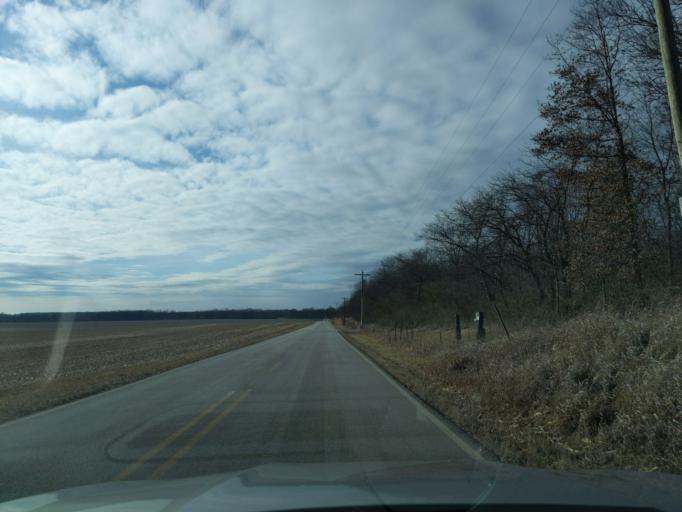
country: US
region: Indiana
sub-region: Tippecanoe County
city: Shadeland
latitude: 40.3375
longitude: -86.9682
